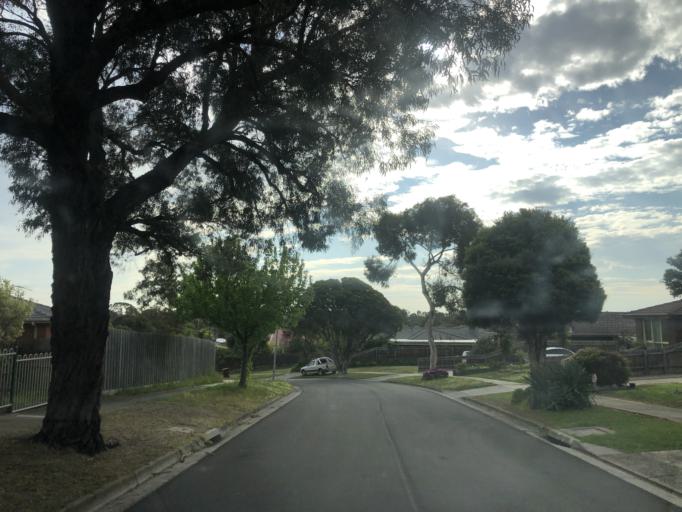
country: AU
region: Victoria
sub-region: Casey
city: Hampton Park
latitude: -38.0246
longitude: 145.2528
